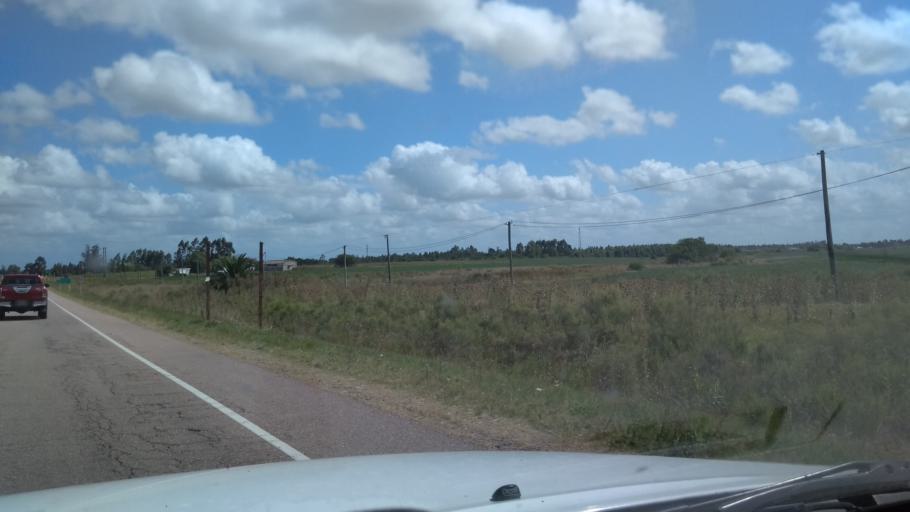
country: UY
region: Canelones
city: Sauce
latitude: -34.6338
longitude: -56.0520
